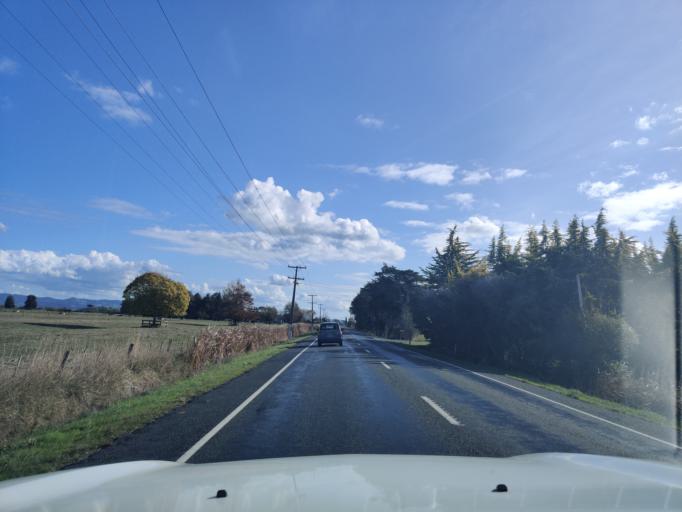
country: NZ
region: Waikato
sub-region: Hauraki District
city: Ngatea
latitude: -37.3111
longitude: 175.5725
